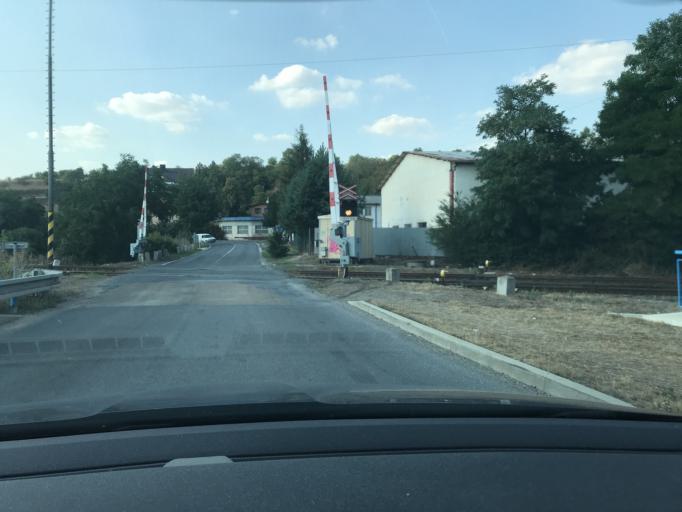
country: CZ
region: Central Bohemia
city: Kralupy nad Vltavou
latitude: 50.2316
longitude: 14.2803
